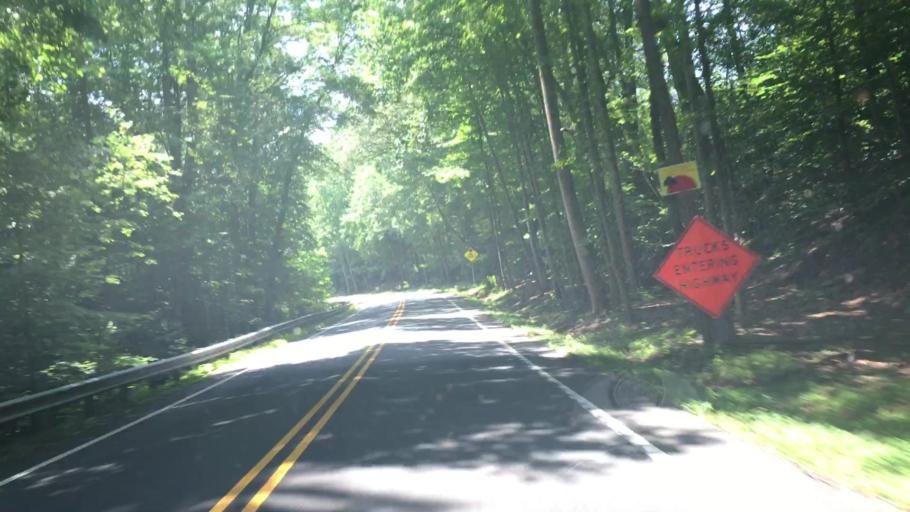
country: US
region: Virginia
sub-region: King George County
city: Passapatanzy
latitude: 38.3011
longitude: -77.2951
